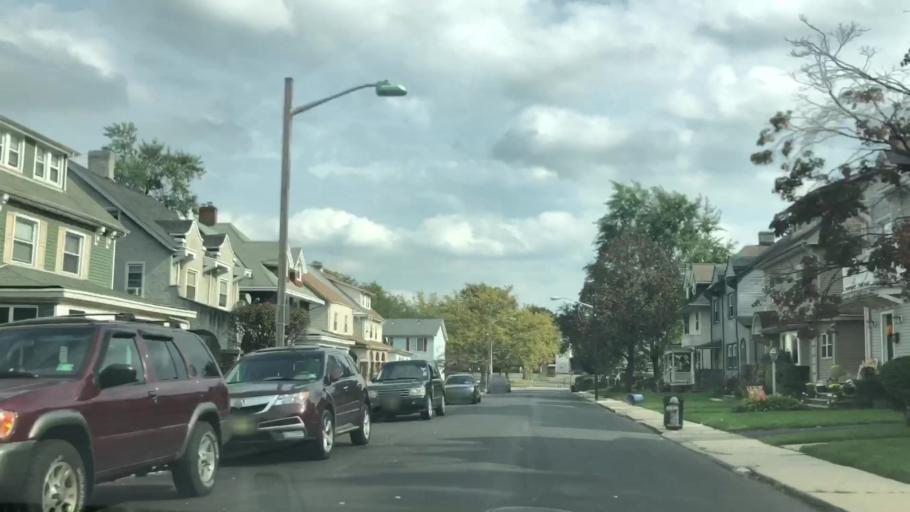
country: US
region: New Jersey
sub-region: Essex County
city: East Orange
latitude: 40.7713
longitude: -74.2176
